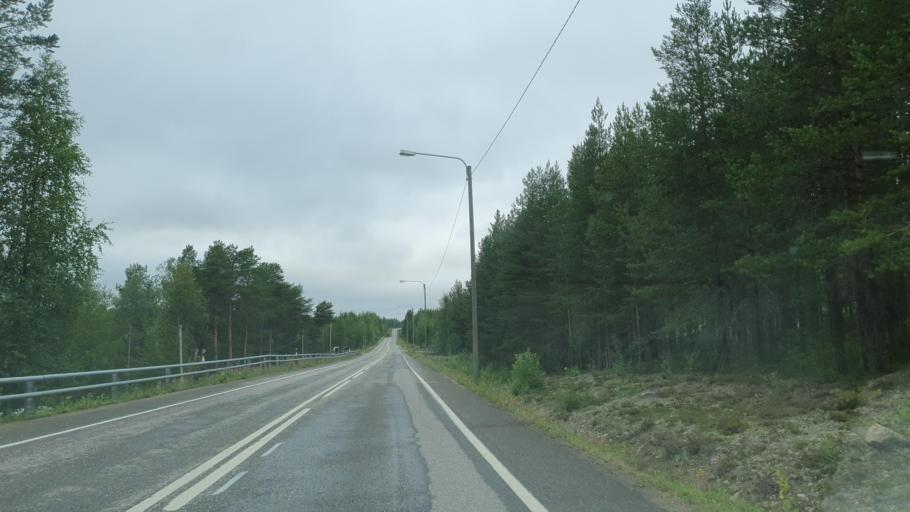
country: FI
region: Lapland
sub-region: Pohjois-Lappi
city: Sodankylae
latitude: 67.3745
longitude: 26.8659
